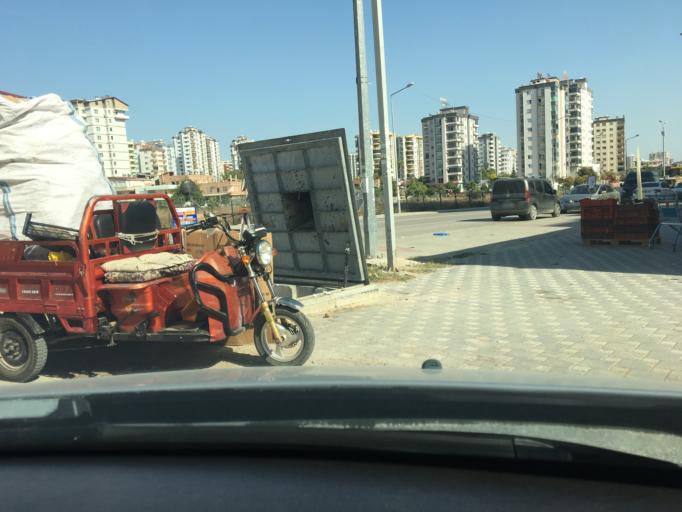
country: TR
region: Adana
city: Seyhan
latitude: 37.0190
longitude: 35.2639
